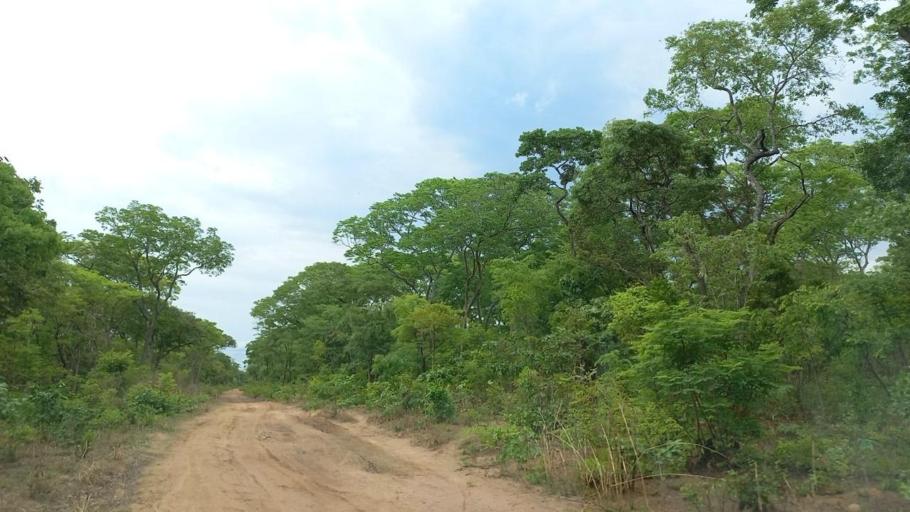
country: ZM
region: North-Western
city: Kalengwa
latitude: -13.5450
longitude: 24.9766
